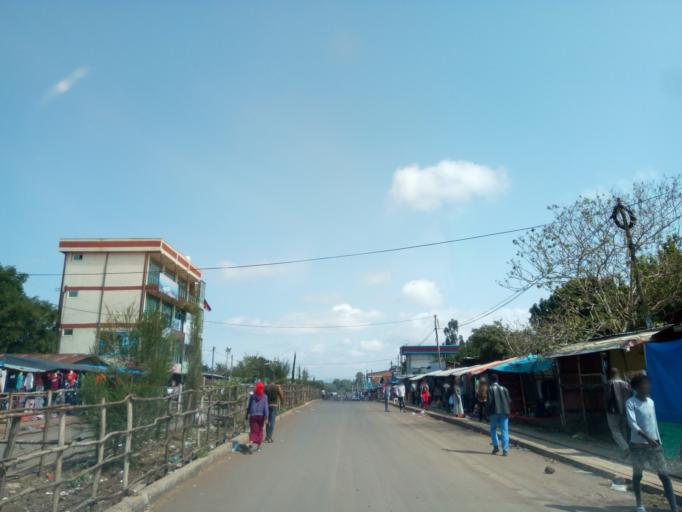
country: ET
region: Oromiya
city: Waliso
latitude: 8.5413
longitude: 37.9720
